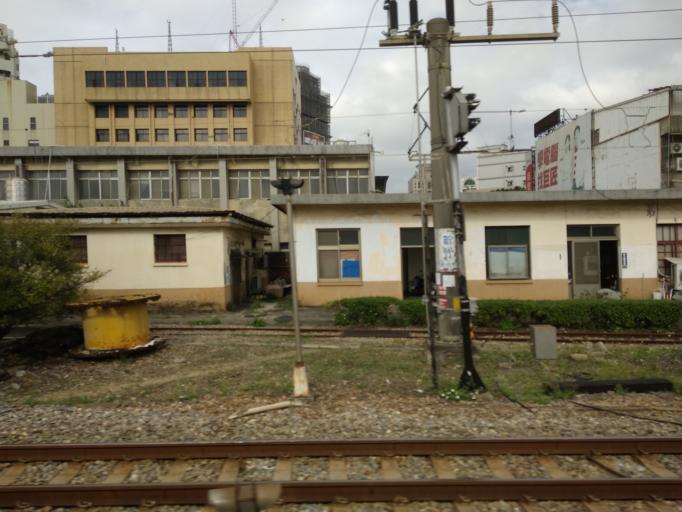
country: TW
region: Taiwan
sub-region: Hsinchu
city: Hsinchu
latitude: 24.8024
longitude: 120.9733
